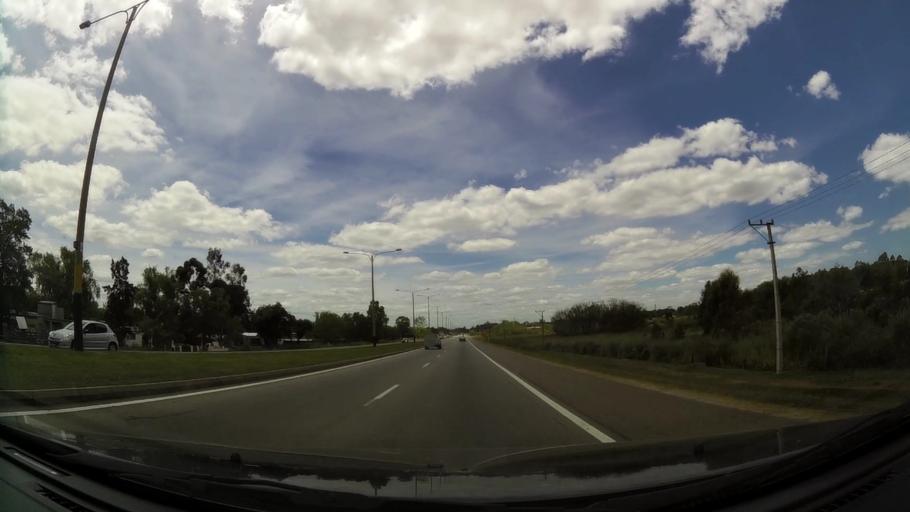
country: UY
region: Canelones
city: Pando
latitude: -34.8039
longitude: -55.9551
